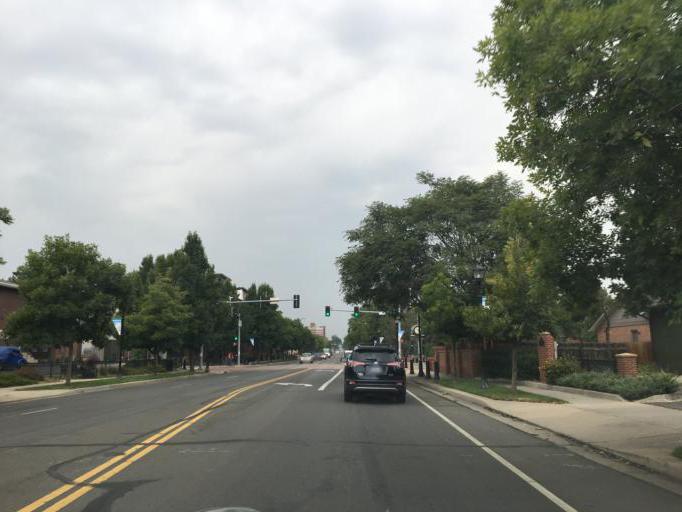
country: US
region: Colorado
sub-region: Jefferson County
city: Edgewater
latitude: 39.7694
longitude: -105.0572
